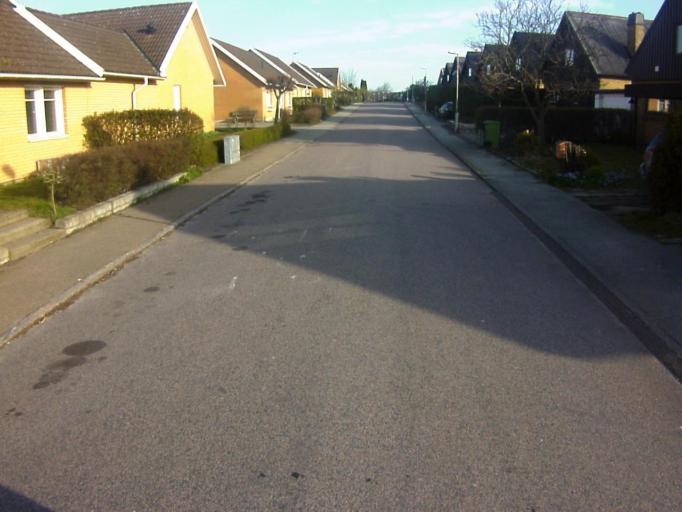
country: SE
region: Skane
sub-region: Kavlinge Kommun
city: Kaevlinge
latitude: 55.7936
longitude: 13.1213
